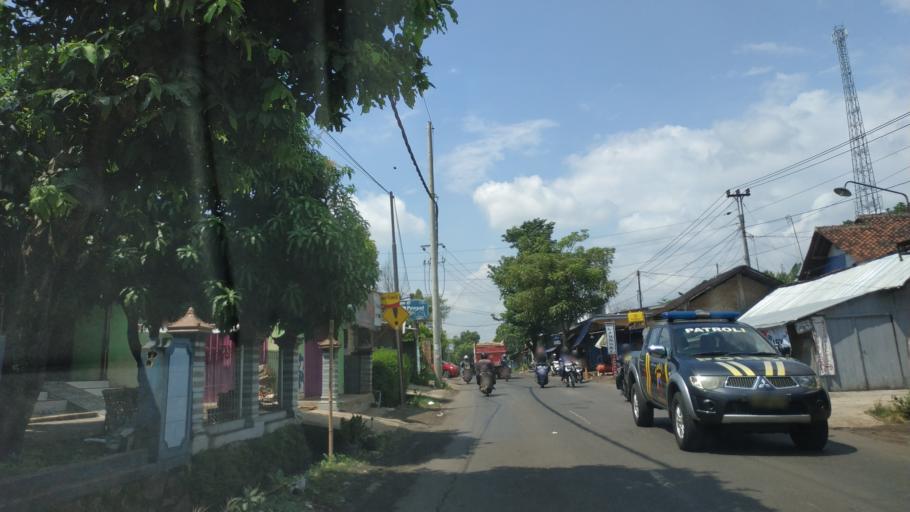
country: ID
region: Central Java
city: Weleri
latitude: -6.9851
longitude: 110.0717
